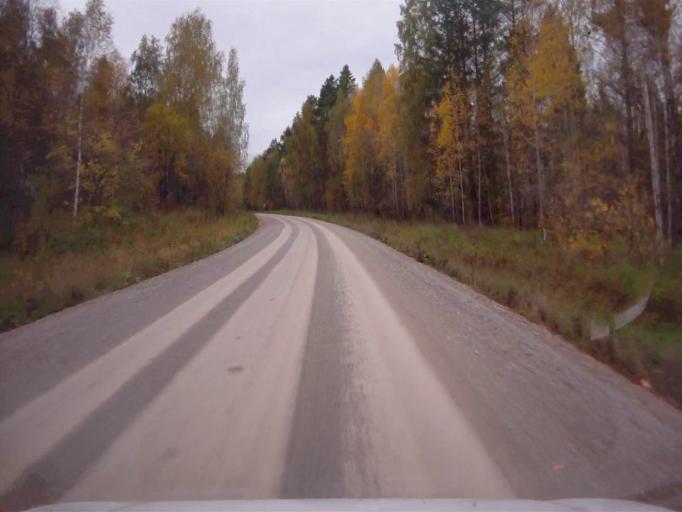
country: RU
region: Chelyabinsk
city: Nyazepetrovsk
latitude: 56.0666
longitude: 59.4380
